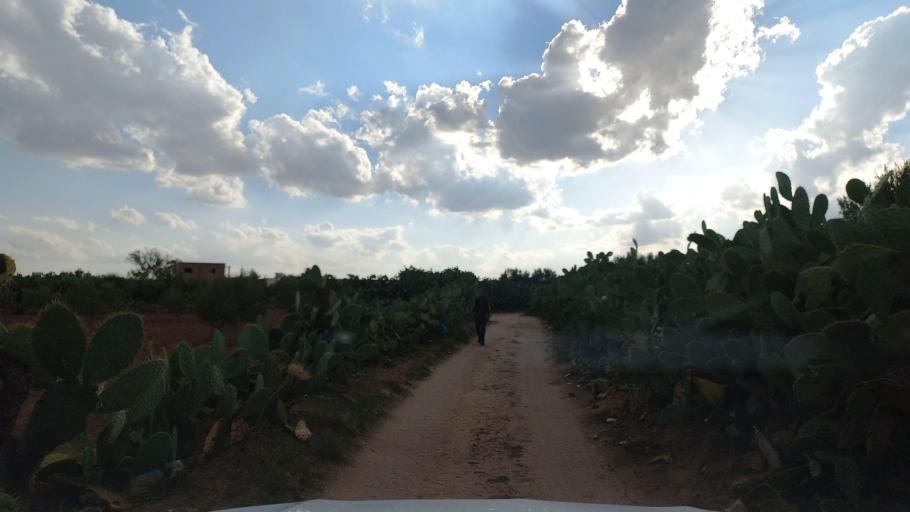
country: TN
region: Al Qasrayn
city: Sbiba
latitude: 35.3846
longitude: 9.0547
